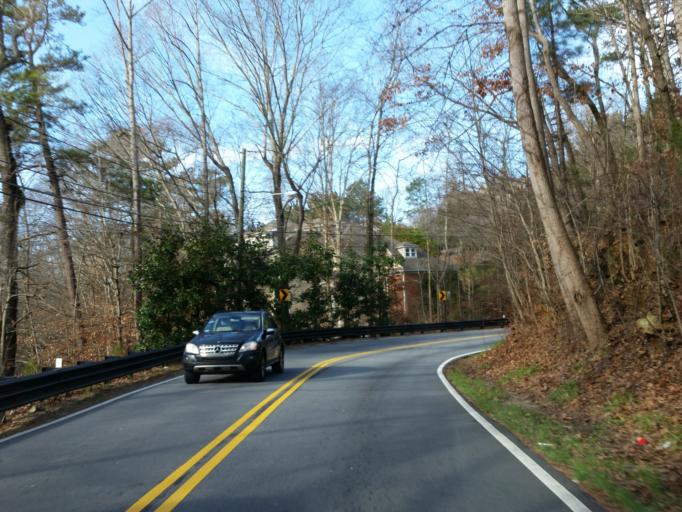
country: US
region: Georgia
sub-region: Fulton County
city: Sandy Springs
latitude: 33.9421
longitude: -84.4377
